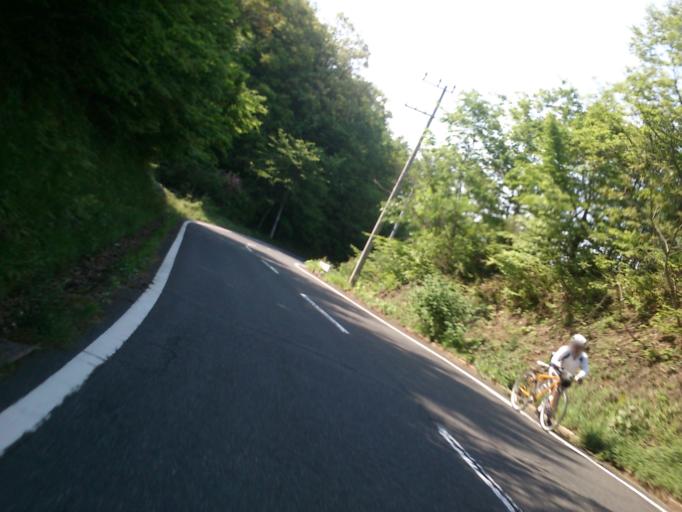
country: JP
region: Kyoto
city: Miyazu
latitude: 35.7264
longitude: 135.1866
